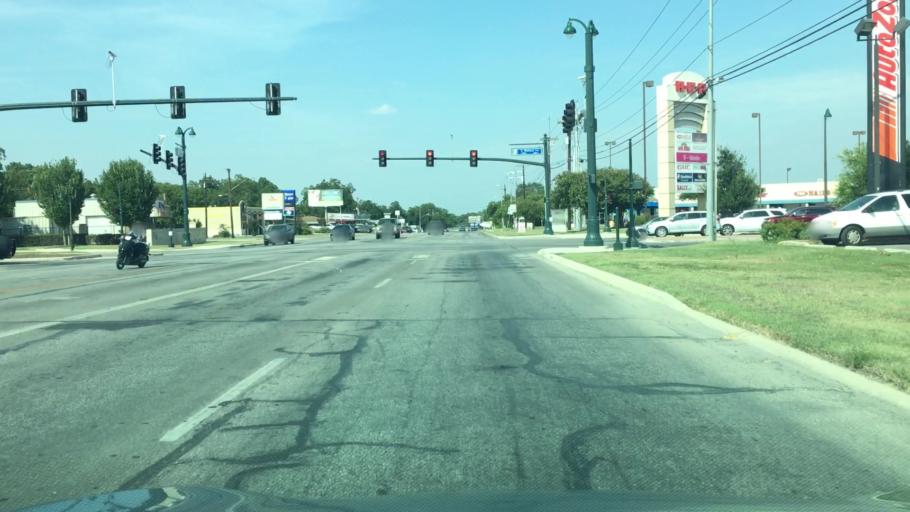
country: US
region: Texas
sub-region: Comal County
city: New Braunfels
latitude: 29.6893
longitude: -98.1281
